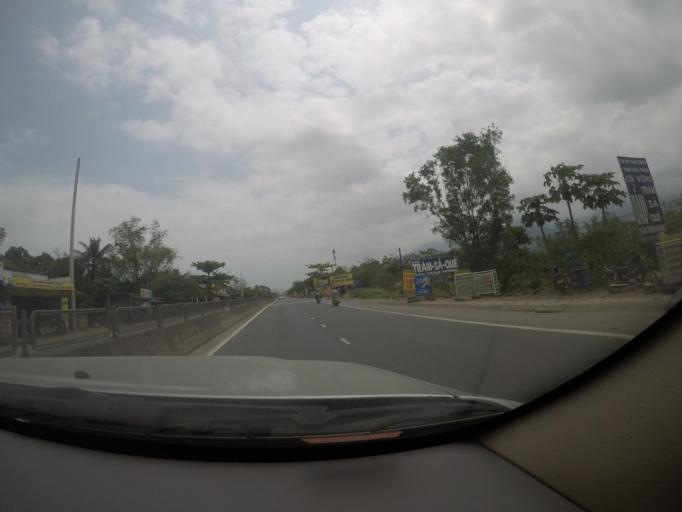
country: VN
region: Thua Thien-Hue
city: Phu Loc
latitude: 16.2727
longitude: 107.9354
